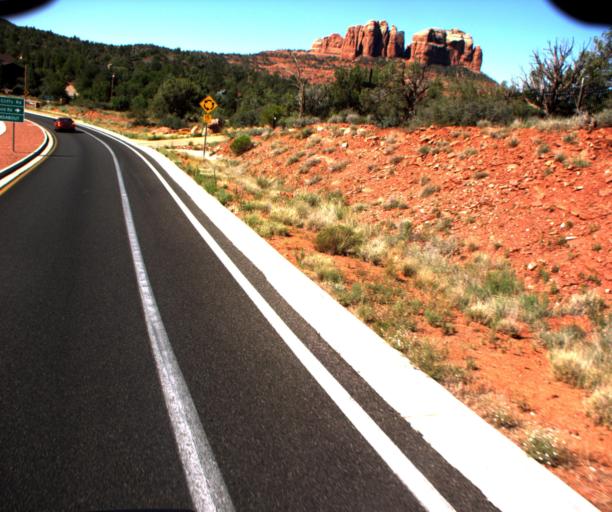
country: US
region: Arizona
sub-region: Coconino County
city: Sedona
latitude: 34.8278
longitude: -111.7783
